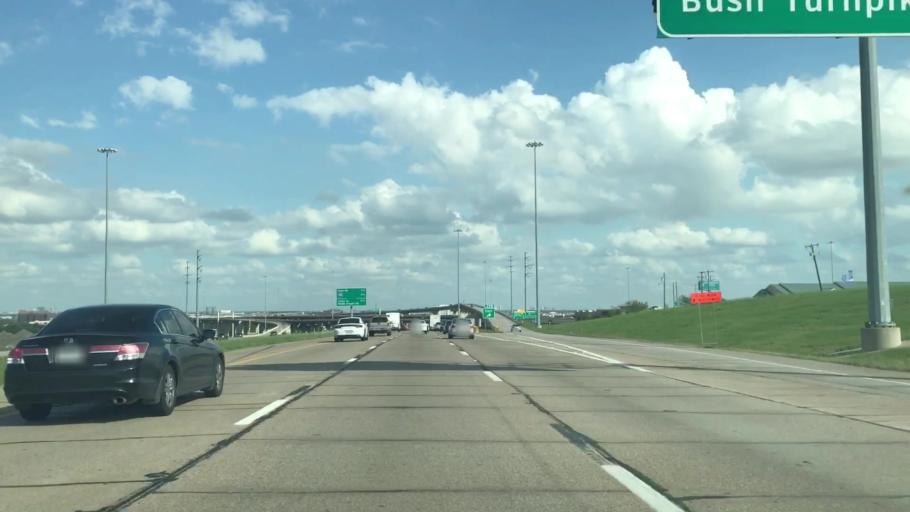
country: US
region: Texas
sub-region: Dallas County
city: Farmers Branch
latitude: 32.9135
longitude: -96.9515
